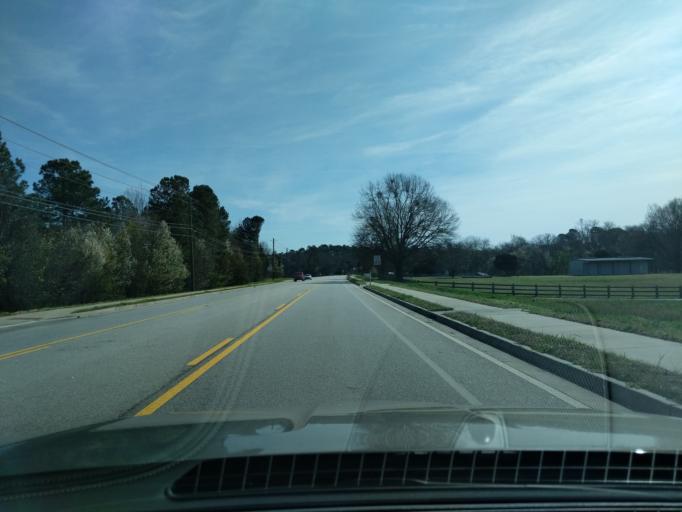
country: US
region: Georgia
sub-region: Columbia County
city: Evans
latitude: 33.5300
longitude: -82.1553
